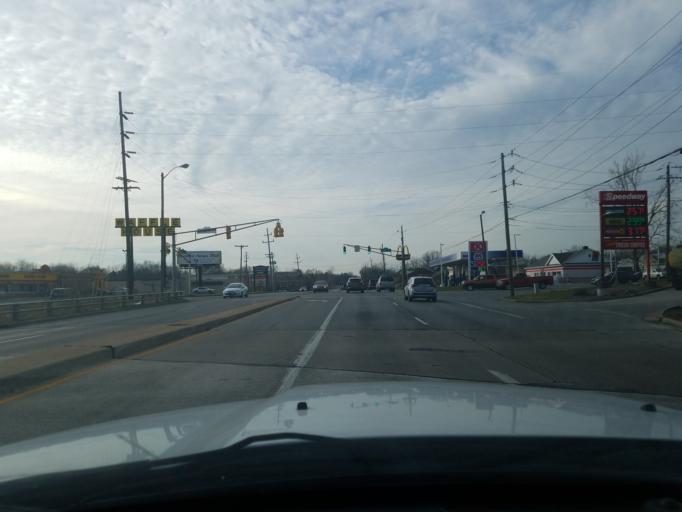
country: US
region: Indiana
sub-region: Marion County
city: Southport
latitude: 39.6656
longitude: -86.0961
